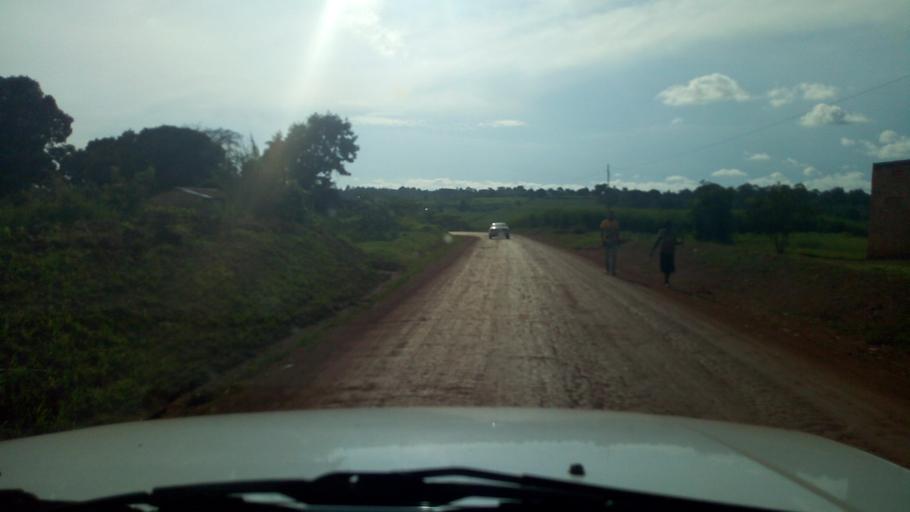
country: UG
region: Western Region
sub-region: Masindi District
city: Masindi
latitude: 1.6743
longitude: 31.6568
